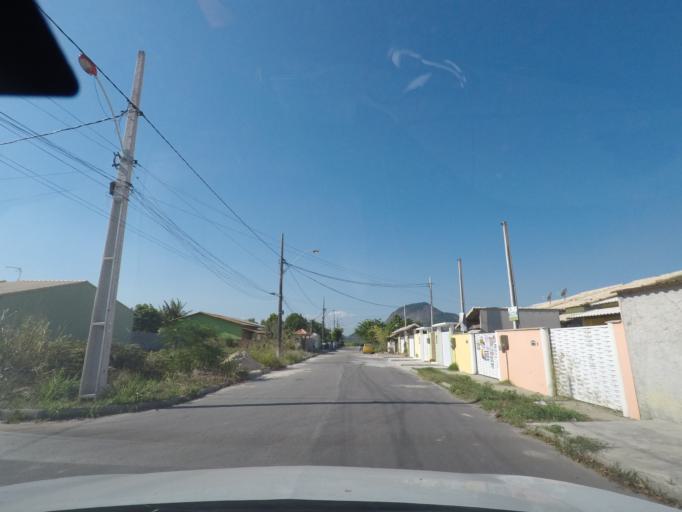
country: BR
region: Rio de Janeiro
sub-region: Marica
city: Marica
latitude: -22.9666
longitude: -42.9199
